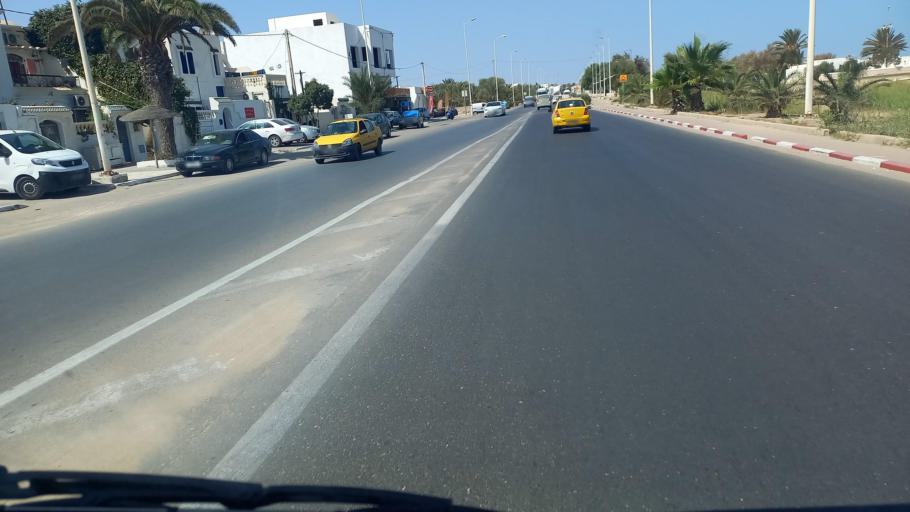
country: TN
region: Madanin
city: Houmt Souk
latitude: 33.8776
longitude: 10.8818
